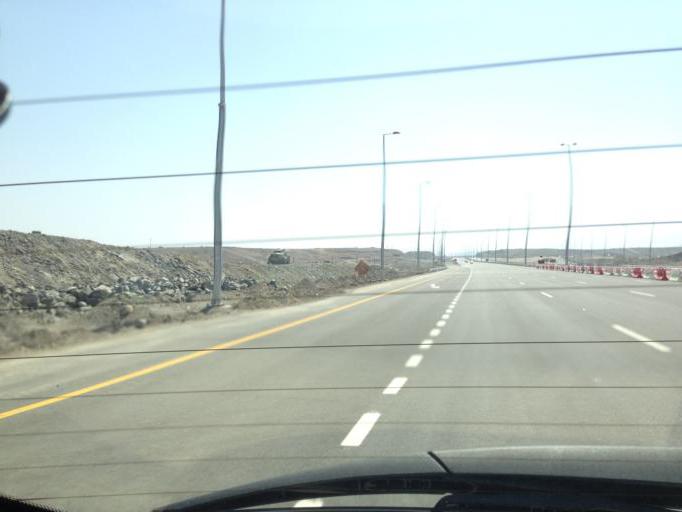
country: OM
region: Al Batinah
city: Rustaq
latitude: 23.5523
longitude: 57.5059
